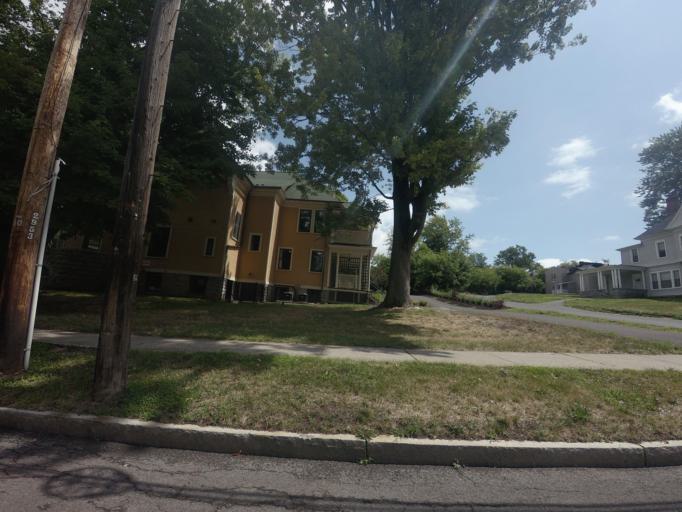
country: US
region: New York
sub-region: Onondaga County
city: Syracuse
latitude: 43.0451
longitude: -76.1196
